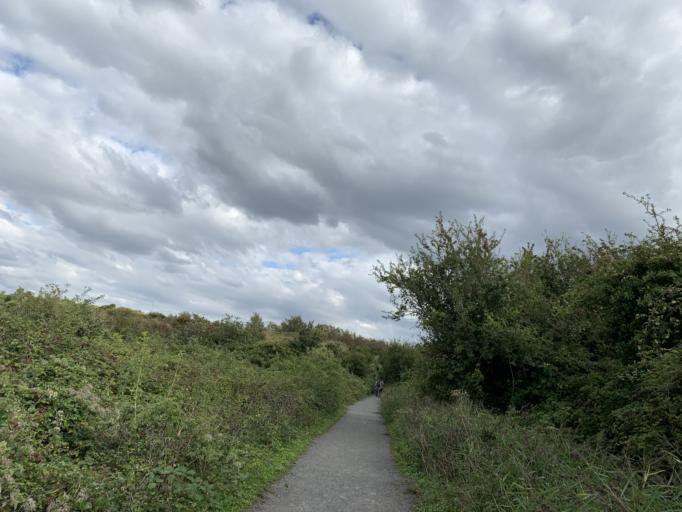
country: GB
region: England
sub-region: Kent
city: Cliffe
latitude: 51.4615
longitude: 0.4816
